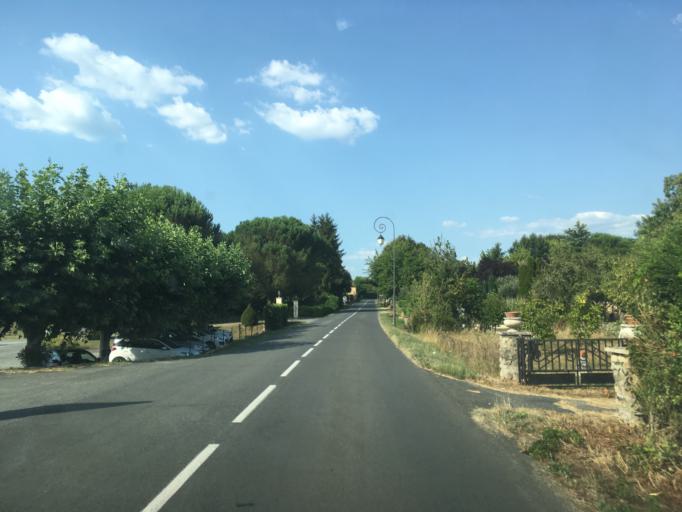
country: FR
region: Aquitaine
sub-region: Departement de la Dordogne
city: Cenac-et-Saint-Julien
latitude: 44.8299
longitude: 1.1621
